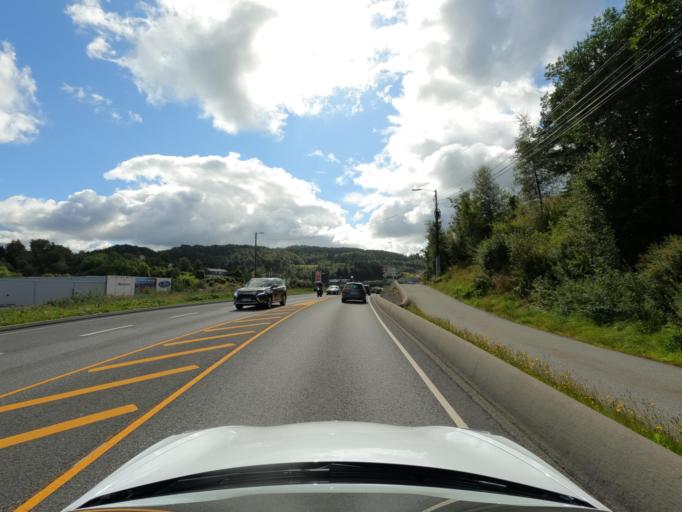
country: NO
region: Hordaland
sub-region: Bergen
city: Hylkje
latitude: 60.4858
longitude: 5.3761
